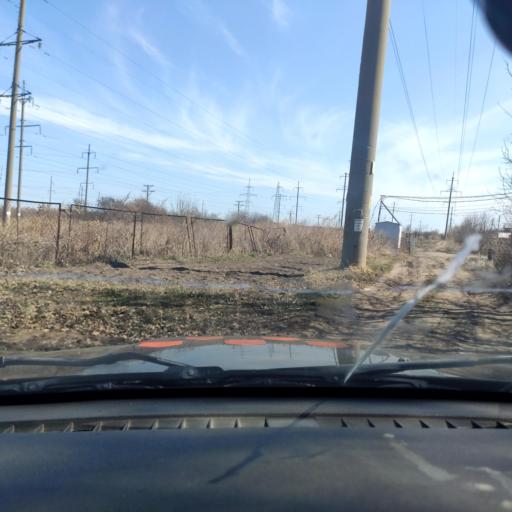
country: RU
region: Samara
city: Tol'yatti
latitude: 53.5871
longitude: 49.3143
